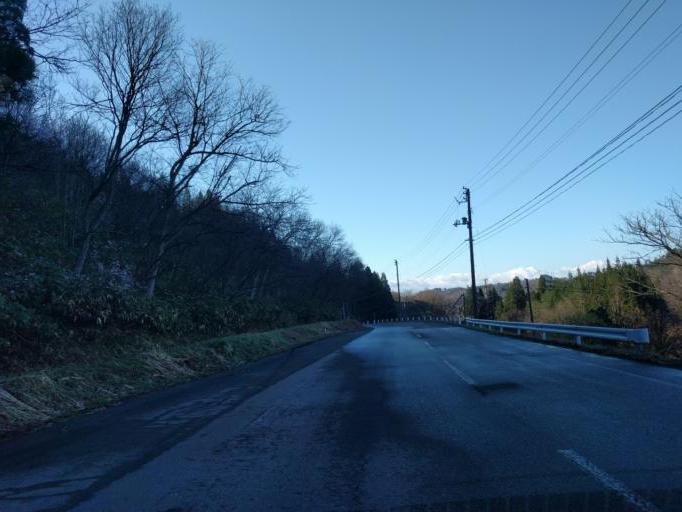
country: JP
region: Fukushima
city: Kitakata
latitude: 37.6967
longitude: 139.7902
